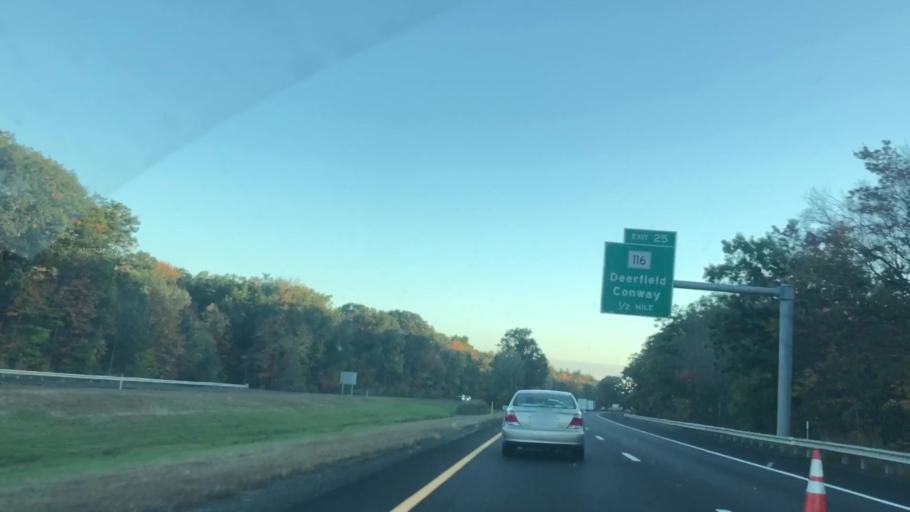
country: US
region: Massachusetts
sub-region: Franklin County
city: South Deerfield
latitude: 42.4936
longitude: -72.6168
